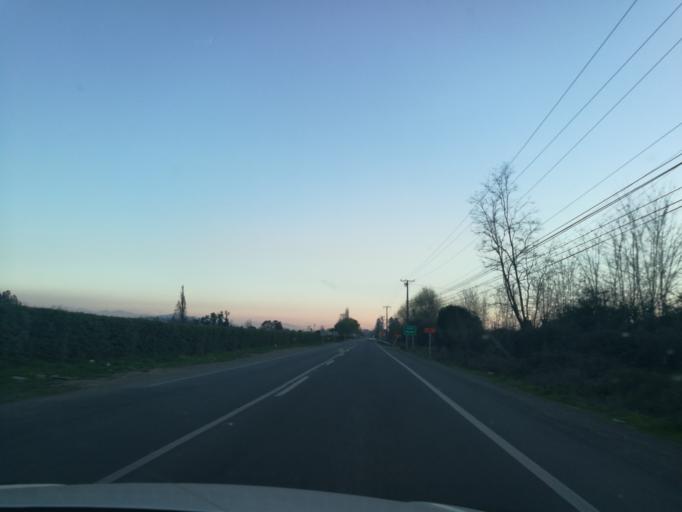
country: CL
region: O'Higgins
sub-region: Provincia de Cachapoal
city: Graneros
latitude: -34.0542
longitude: -70.7267
